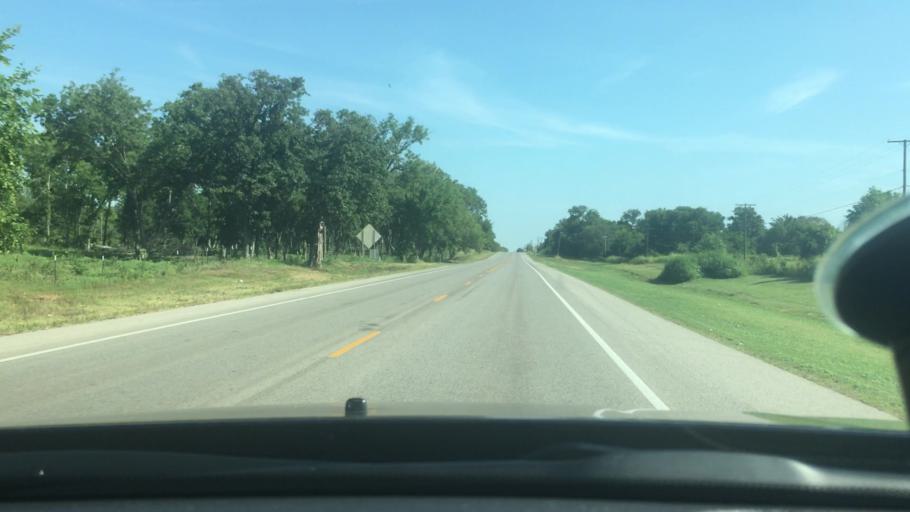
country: US
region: Oklahoma
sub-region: Garvin County
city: Pauls Valley
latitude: 34.6976
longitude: -97.2128
